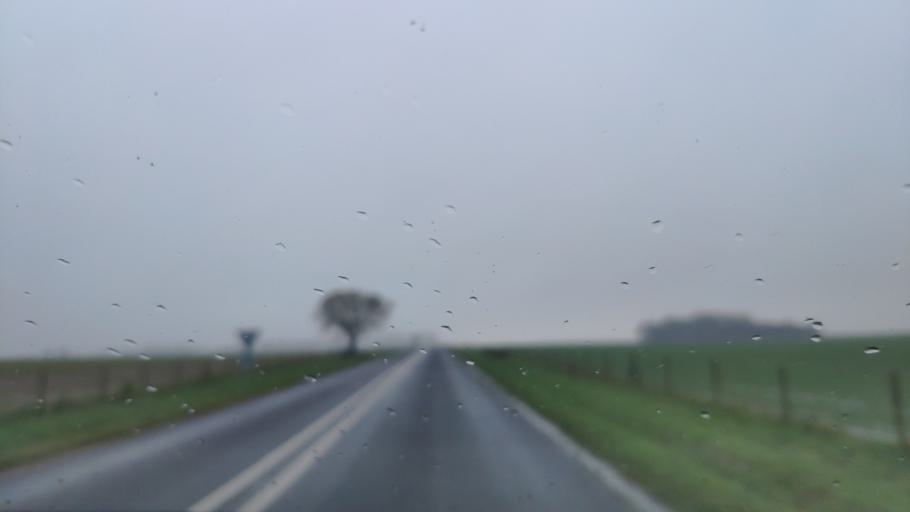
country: FR
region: Haute-Normandie
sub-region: Departement de la Seine-Maritime
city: Doudeville
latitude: 49.7624
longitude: 0.7704
